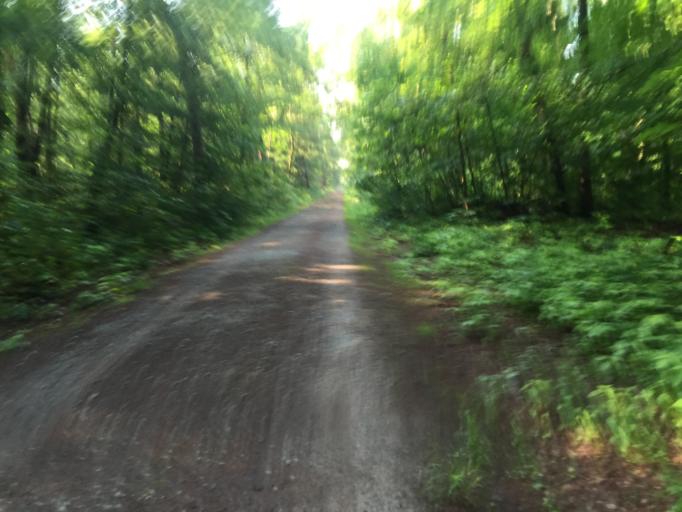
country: DE
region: Hesse
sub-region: Regierungsbezirk Darmstadt
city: Darmstadt
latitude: 49.8513
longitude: 8.6142
